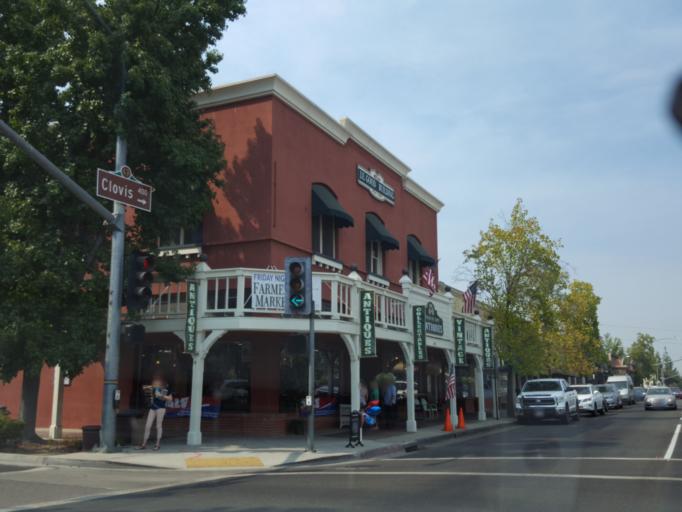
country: US
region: California
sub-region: Fresno County
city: Clovis
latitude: 36.8238
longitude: -119.7007
